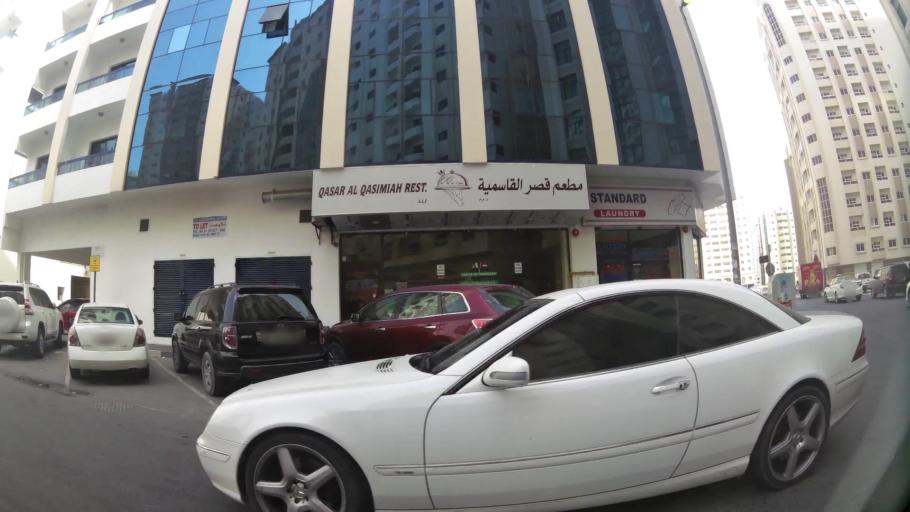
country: AE
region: Ash Shariqah
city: Sharjah
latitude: 25.3448
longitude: 55.3891
